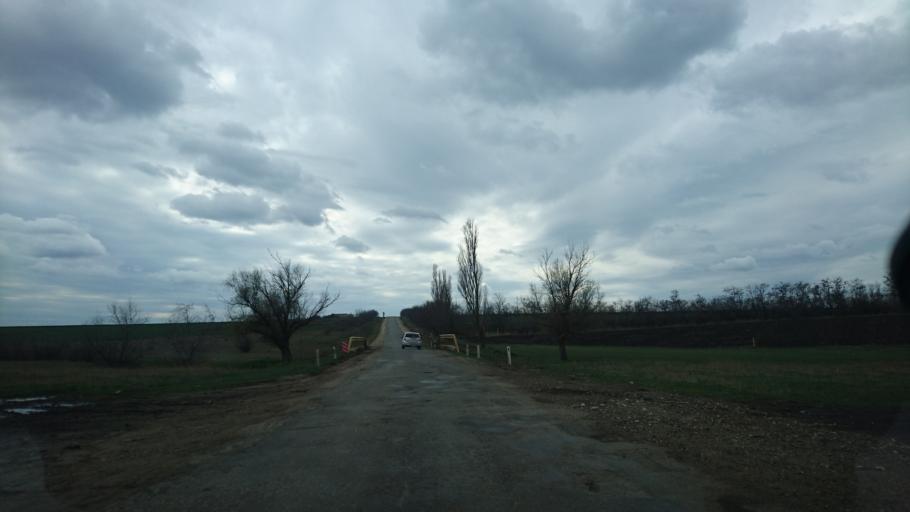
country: MD
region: Gagauzia
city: Comrat
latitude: 46.3111
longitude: 28.5853
